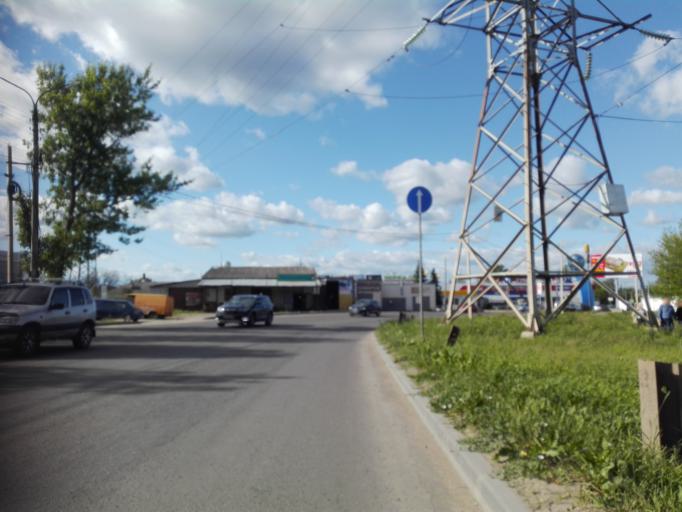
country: RU
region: Orjol
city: Orel
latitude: 52.9453
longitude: 36.0318
